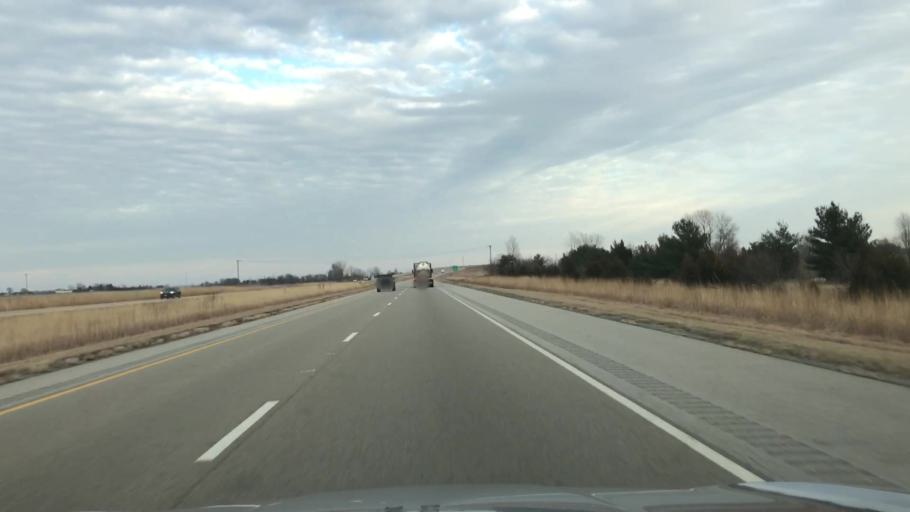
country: US
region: Illinois
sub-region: Logan County
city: Lincoln
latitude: 40.1835
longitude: -89.3337
